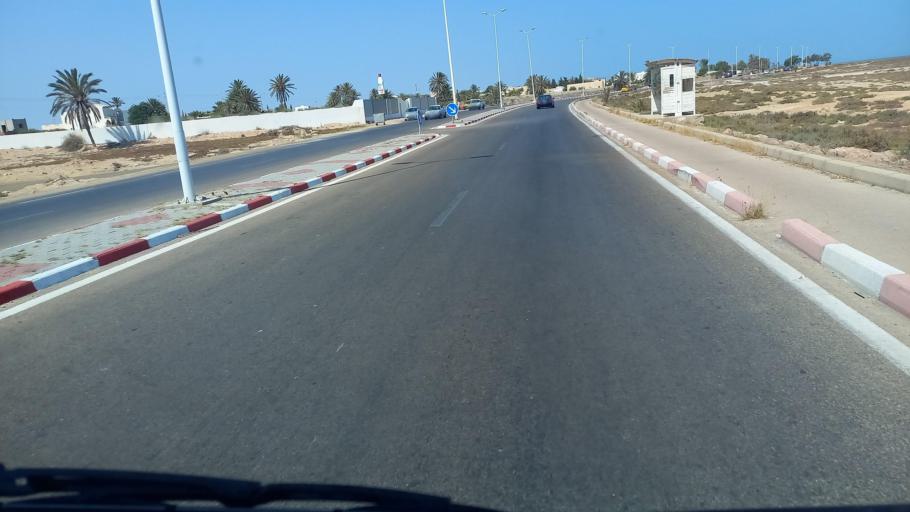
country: TN
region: Madanin
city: Midoun
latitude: 33.8696
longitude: 10.9394
